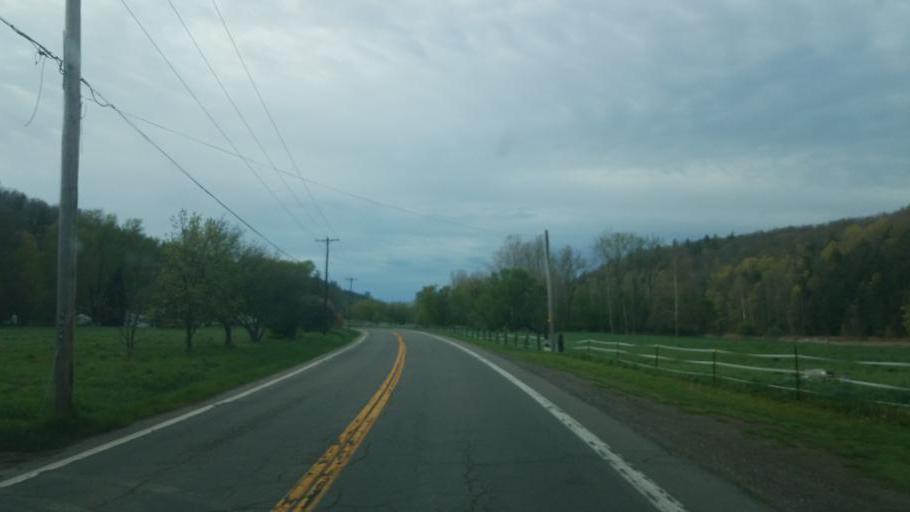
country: US
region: New York
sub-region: Steuben County
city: Canisteo
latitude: 42.2439
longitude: -77.5835
